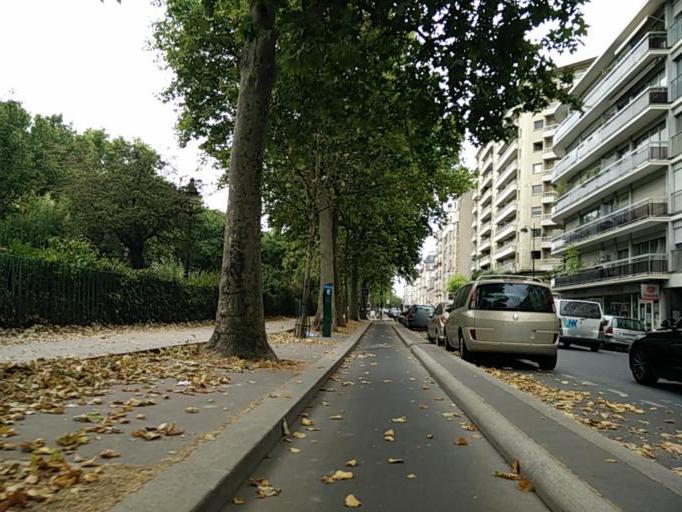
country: FR
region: Ile-de-France
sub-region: Paris
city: Paris
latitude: 48.8575
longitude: 2.3708
